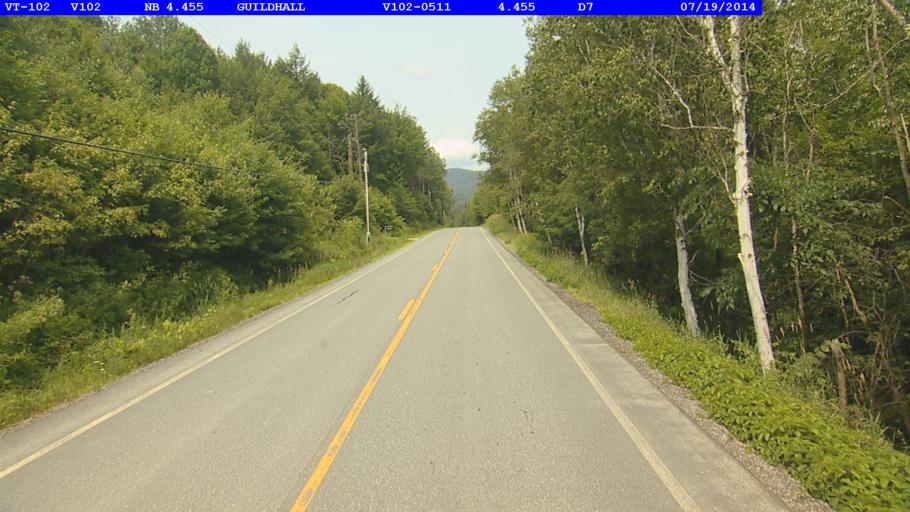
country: US
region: Vermont
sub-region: Essex County
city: Guildhall
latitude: 44.5522
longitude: -71.5957
